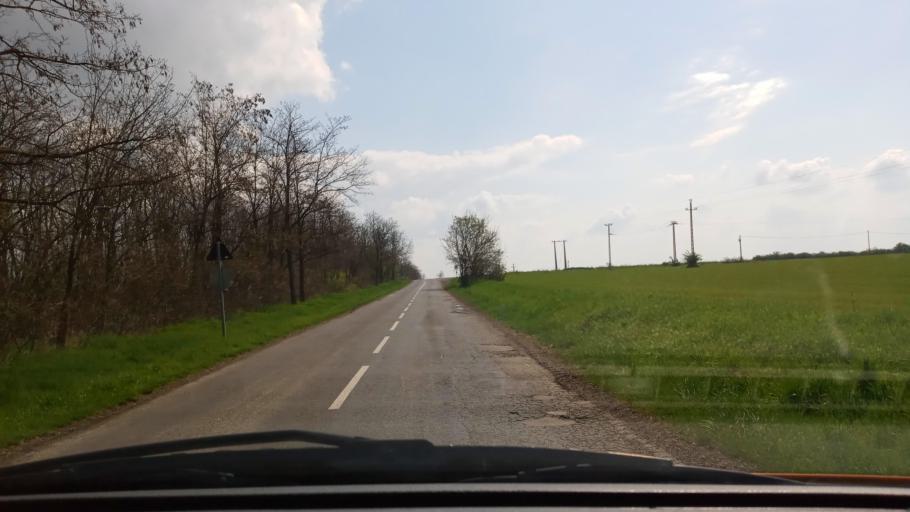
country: HU
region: Baranya
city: Pecsvarad
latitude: 46.1079
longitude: 18.4937
